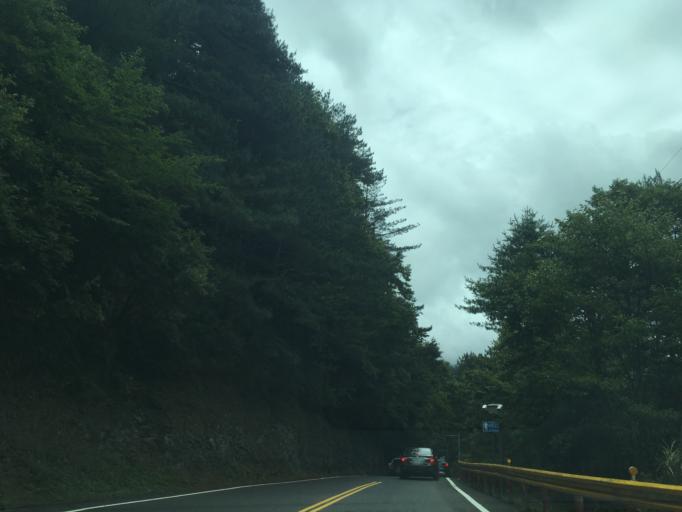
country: TW
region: Taiwan
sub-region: Hualien
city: Hualian
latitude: 24.1804
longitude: 121.3126
